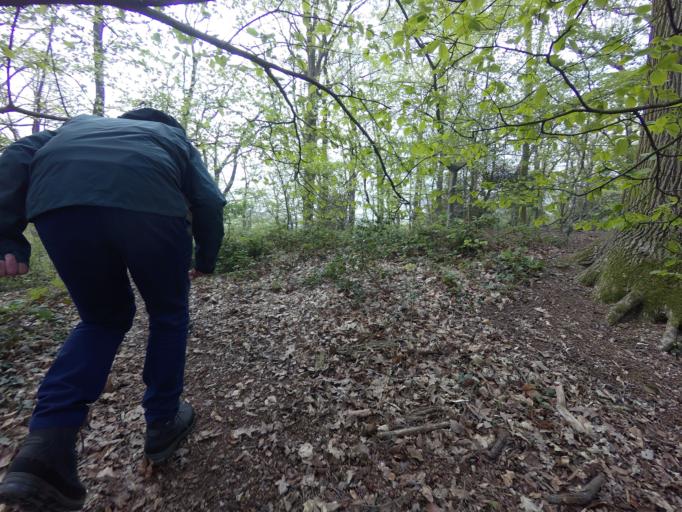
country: NL
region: Limburg
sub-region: Gemeente Schinnen
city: Schinnen
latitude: 50.9413
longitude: 5.8921
